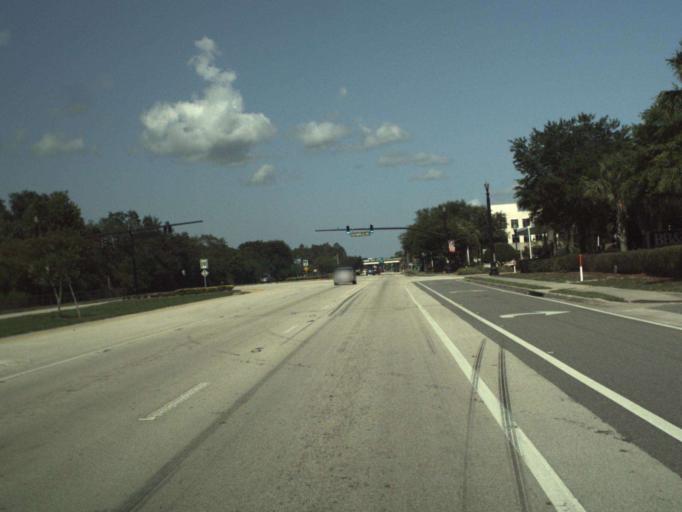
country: US
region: Florida
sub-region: Seminole County
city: Oviedo
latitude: 28.6900
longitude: -81.2350
